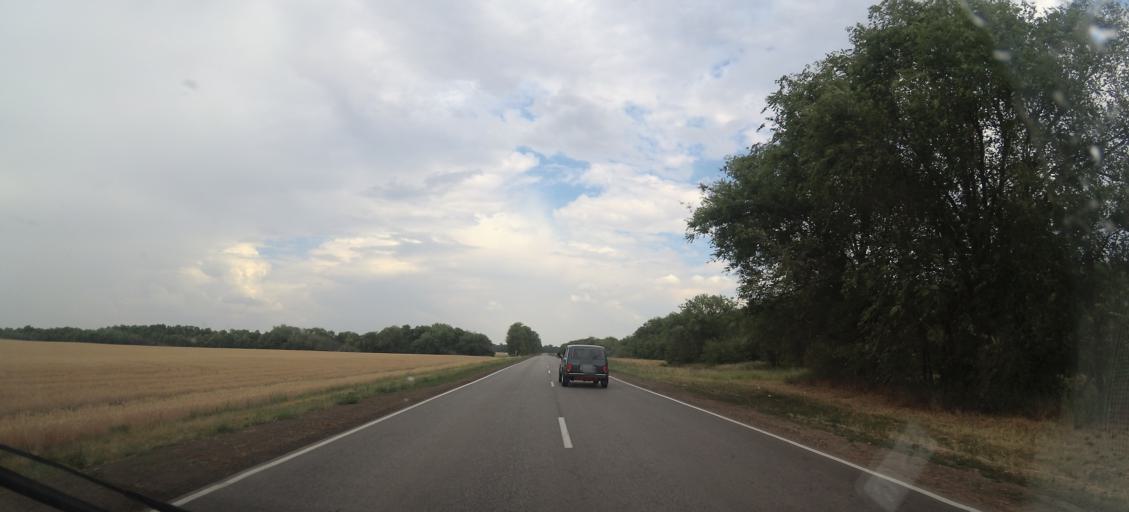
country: RU
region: Rostov
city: Peschanokopskoye
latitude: 46.2012
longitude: 41.1879
